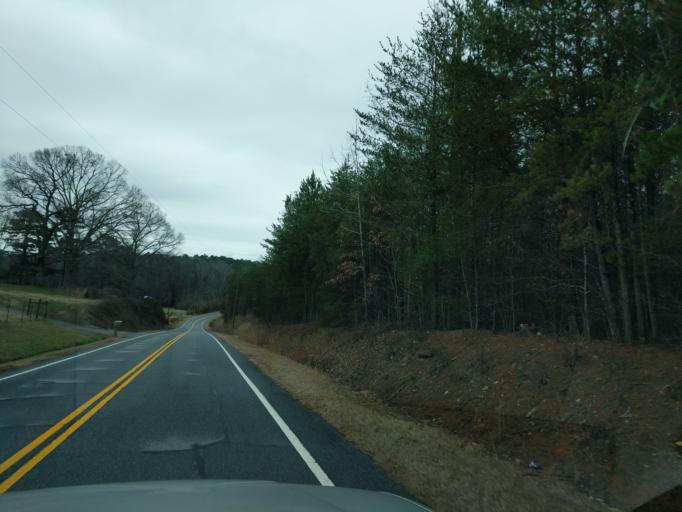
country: US
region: South Carolina
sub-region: Oconee County
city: Walhalla
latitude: 34.7976
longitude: -83.0777
